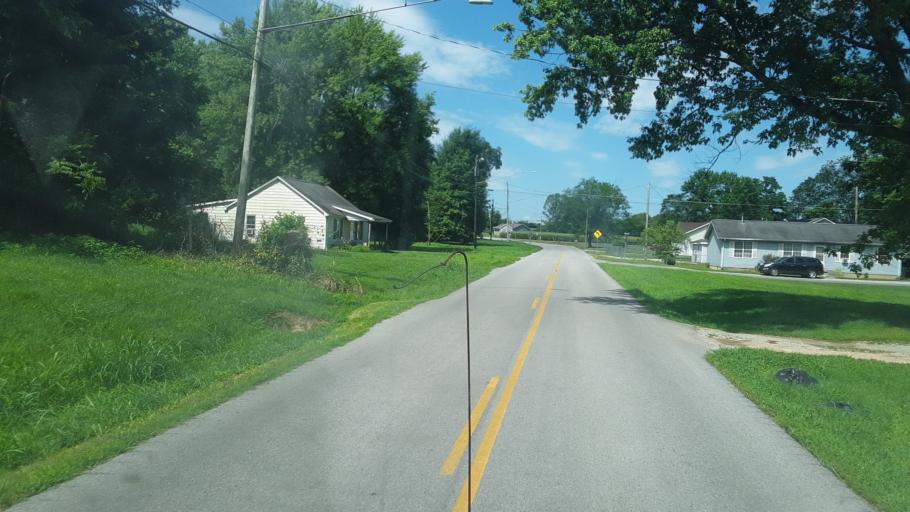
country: US
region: Kentucky
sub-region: Christian County
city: Oak Grove
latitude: 36.7822
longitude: -87.3477
